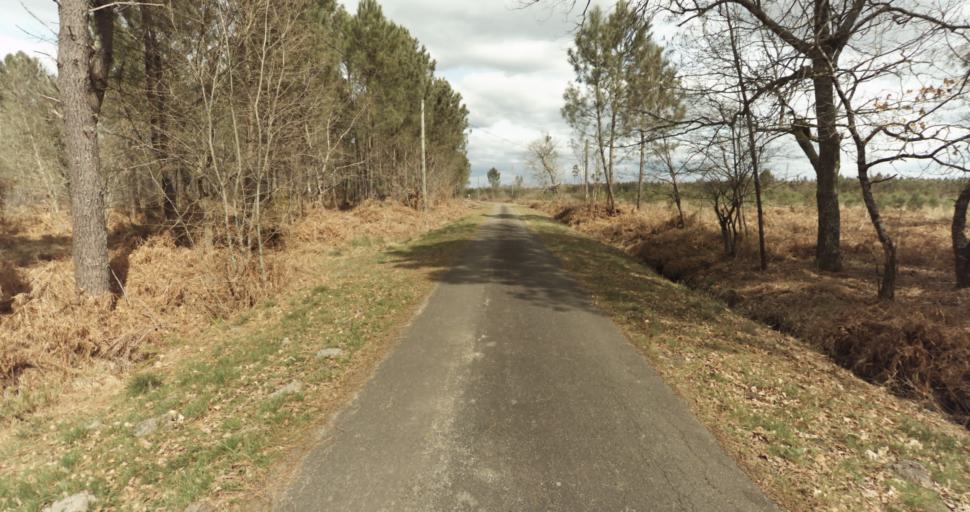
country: FR
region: Aquitaine
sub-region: Departement des Landes
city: Roquefort
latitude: 44.0821
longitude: -0.3921
